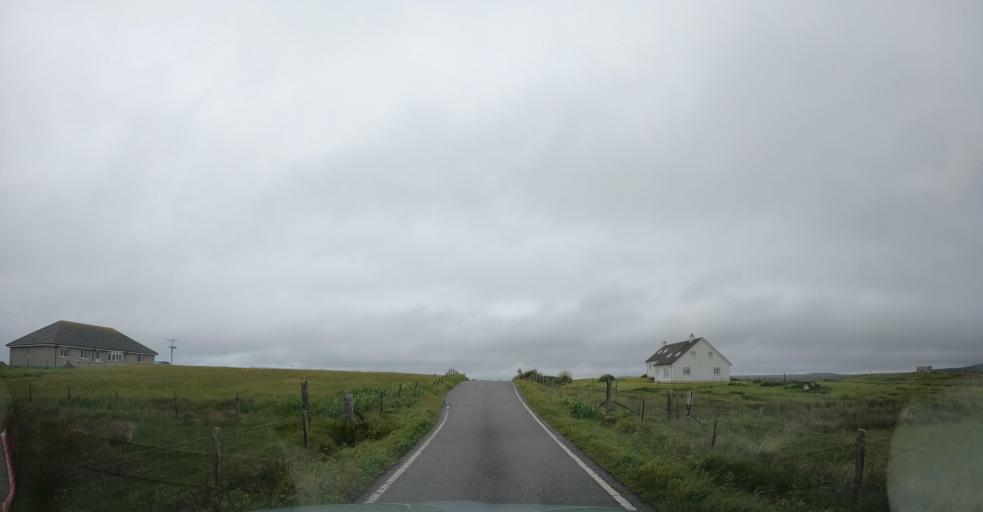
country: GB
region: Scotland
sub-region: Eilean Siar
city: Isle of North Uist
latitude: 57.5628
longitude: -7.3772
